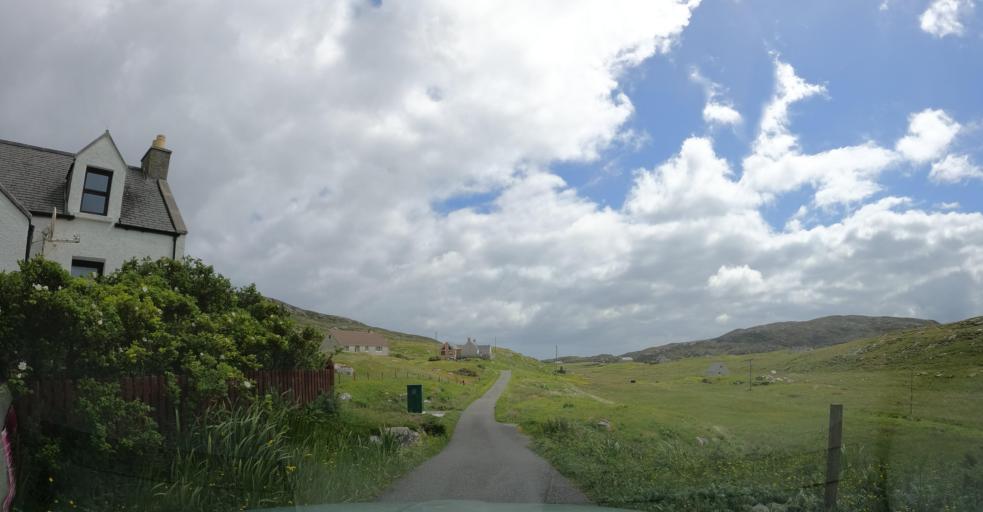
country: GB
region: Scotland
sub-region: Eilean Siar
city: Isle of South Uist
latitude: 57.0719
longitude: -7.2979
